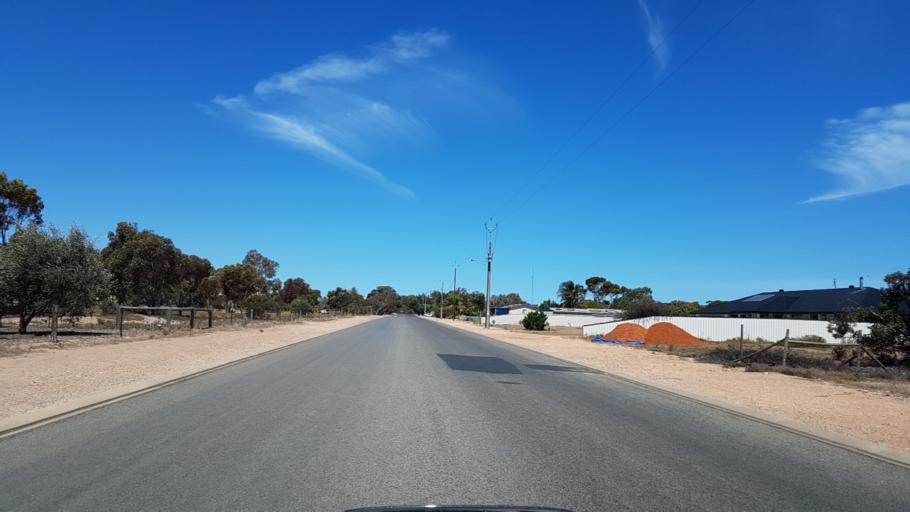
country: AU
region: South Australia
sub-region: Copper Coast
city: Wallaroo
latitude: -34.0567
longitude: 137.5817
